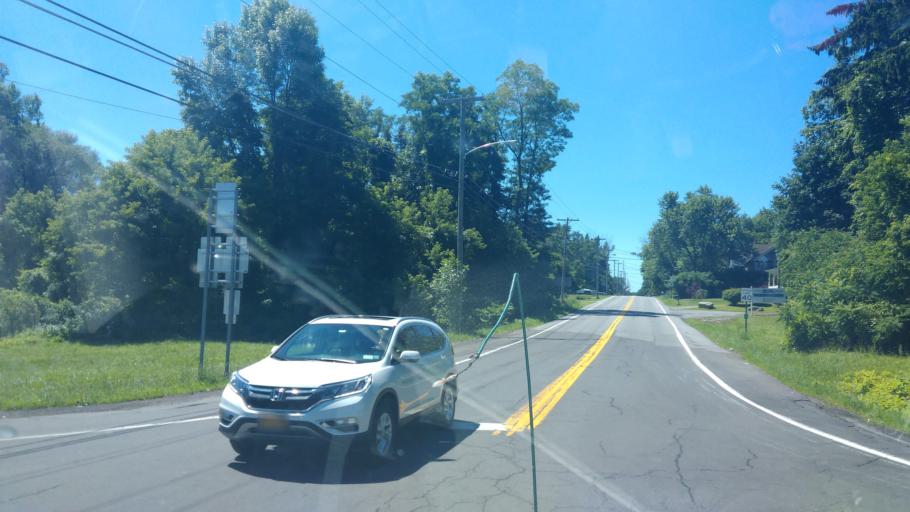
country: US
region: New York
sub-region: Wayne County
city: Sodus
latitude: 43.2063
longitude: -76.9822
